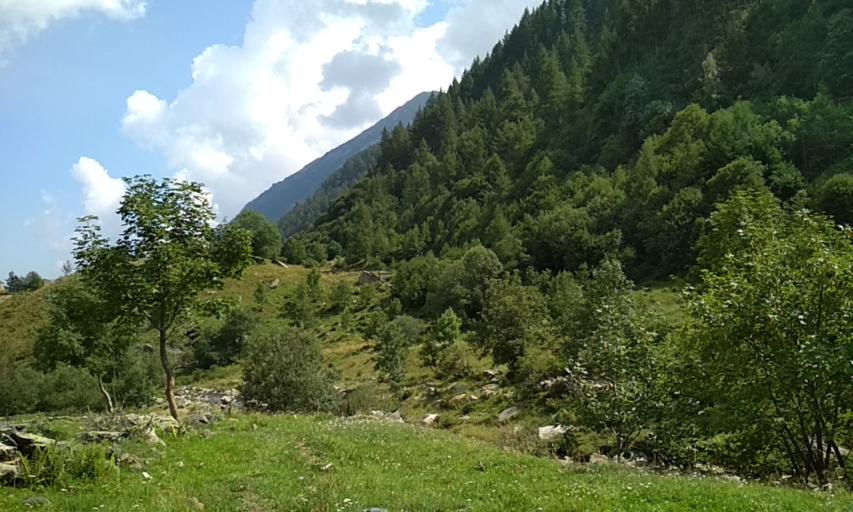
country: IT
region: Piedmont
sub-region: Provincia di Torino
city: Noasca
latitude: 45.4594
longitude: 7.2741
